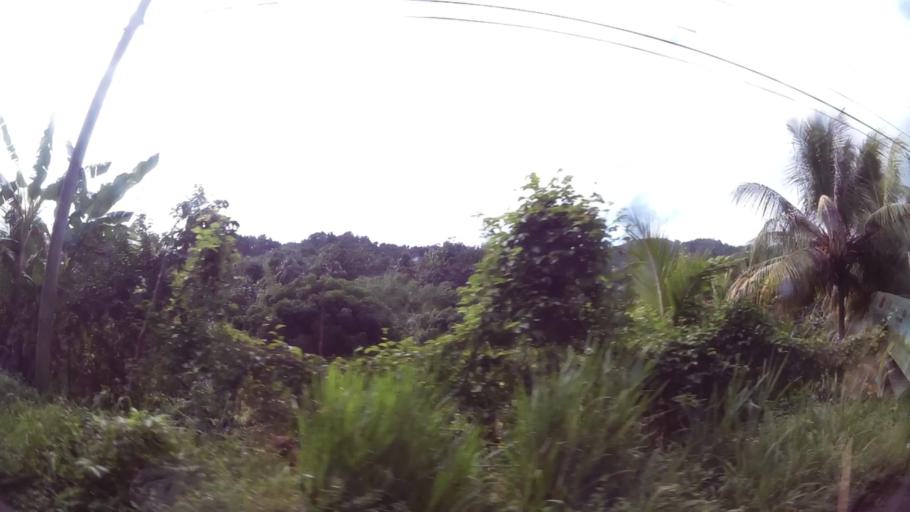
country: DM
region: Saint David
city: Castle Bruce
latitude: 15.4655
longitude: -61.2530
